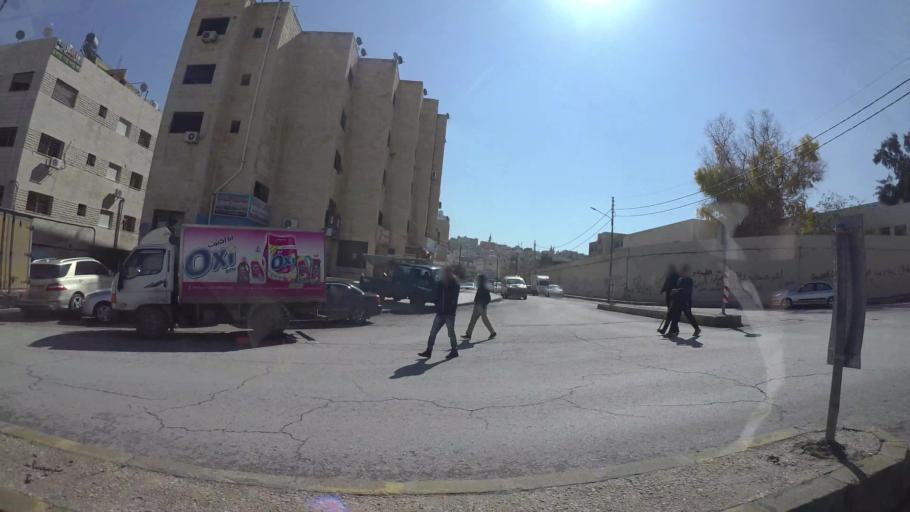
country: JO
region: Amman
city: Amman
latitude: 31.9844
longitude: 35.9810
